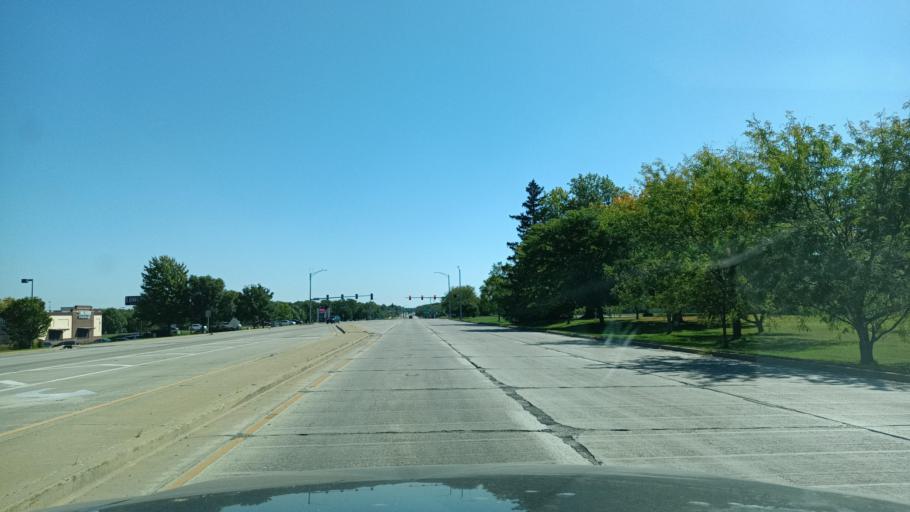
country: US
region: Illinois
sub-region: Peoria County
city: Dunlap
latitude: 40.7776
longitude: -89.6790
